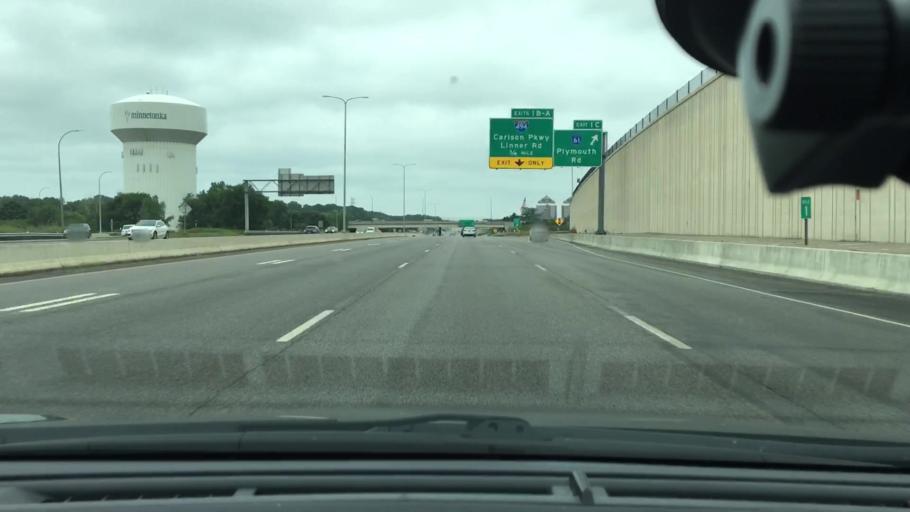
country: US
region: Minnesota
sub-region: Hennepin County
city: Minnetonka Mills
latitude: 44.9713
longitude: -93.4399
